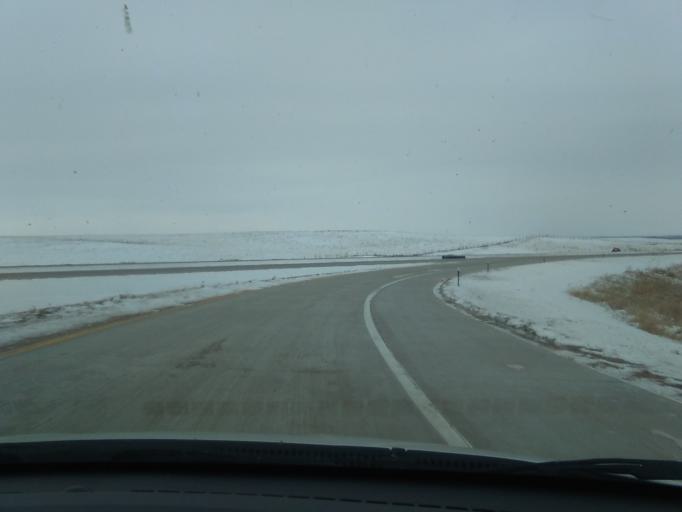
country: US
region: Colorado
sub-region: Sedgwick County
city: Julesburg
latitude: 41.0349
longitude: -102.2099
